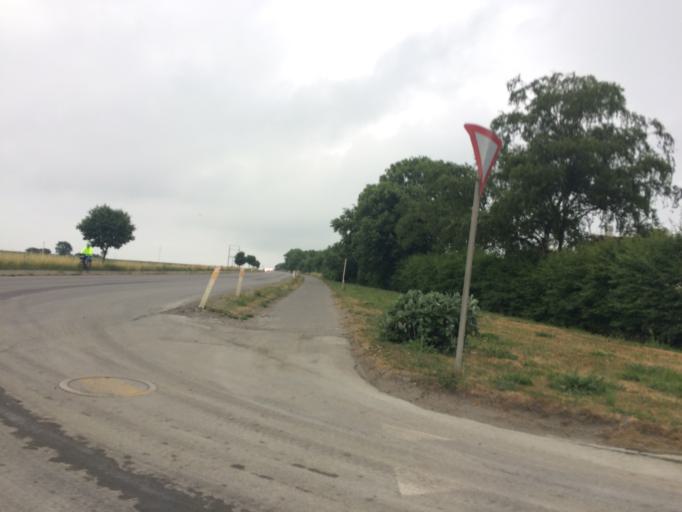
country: DK
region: Capital Region
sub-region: Bornholm Kommune
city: Ronne
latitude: 55.1047
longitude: 14.7336
